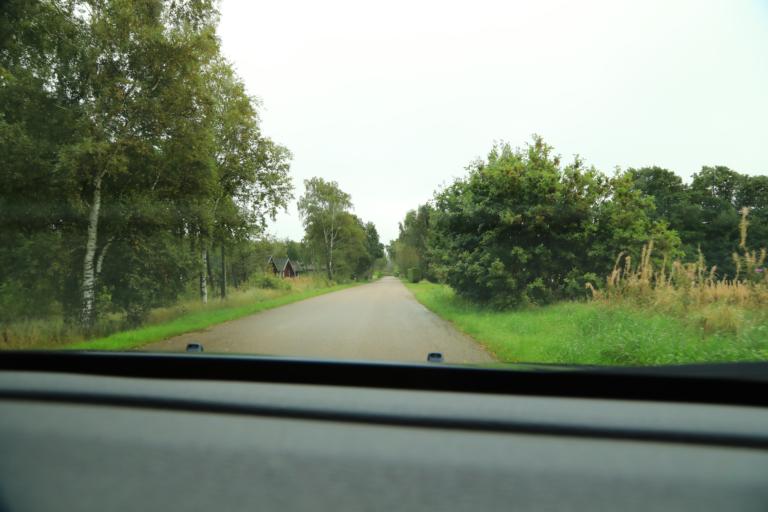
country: SE
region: Halland
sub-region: Varbergs Kommun
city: Tvaaker
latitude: 57.0464
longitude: 12.3544
